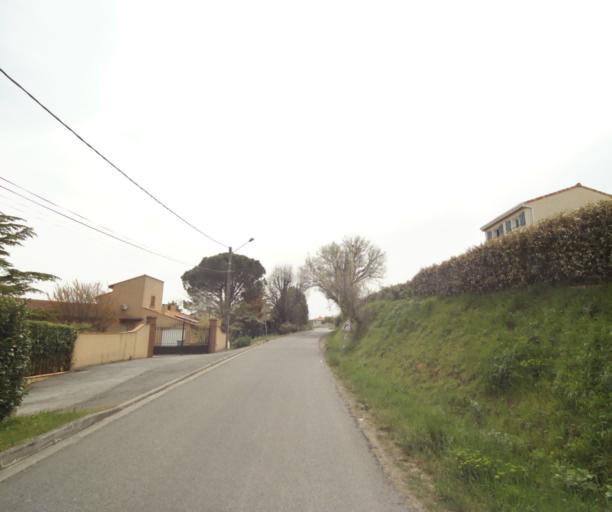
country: FR
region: Midi-Pyrenees
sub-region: Departement de la Haute-Garonne
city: Pechabou
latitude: 43.5040
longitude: 1.5021
